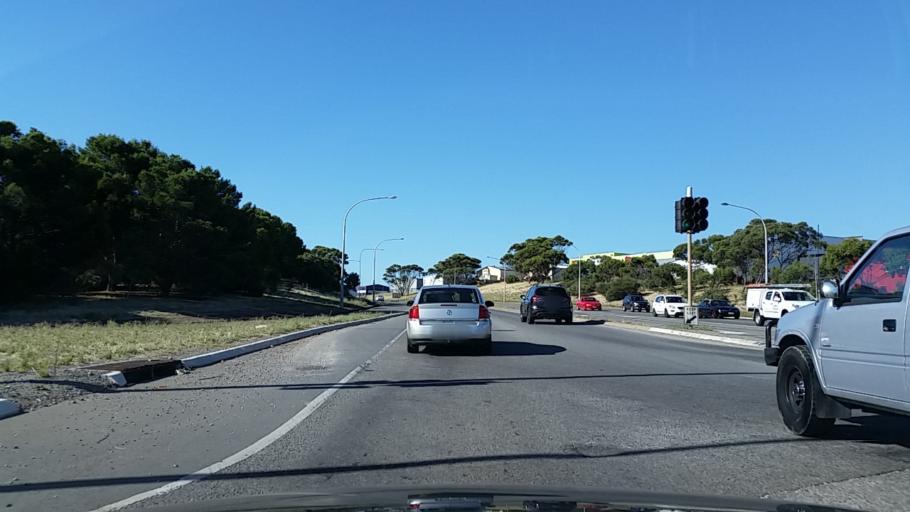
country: AU
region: South Australia
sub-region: Onkaparinga
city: Morphett Vale
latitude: -35.1065
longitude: 138.4989
